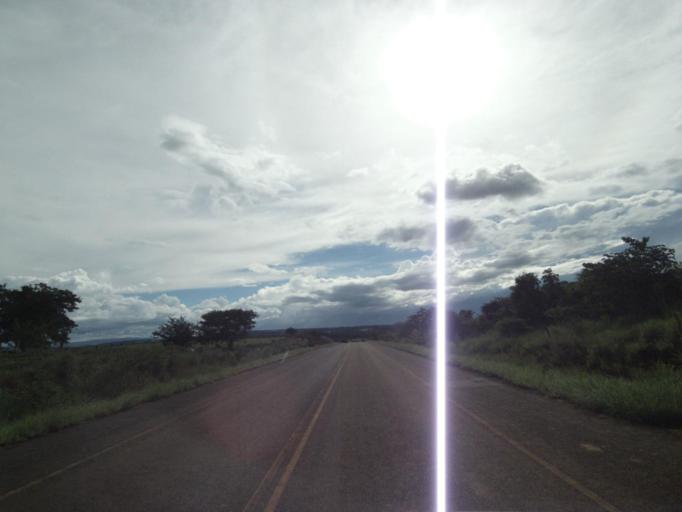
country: BR
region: Goias
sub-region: Jaragua
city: Jaragua
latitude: -15.8679
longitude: -49.4063
